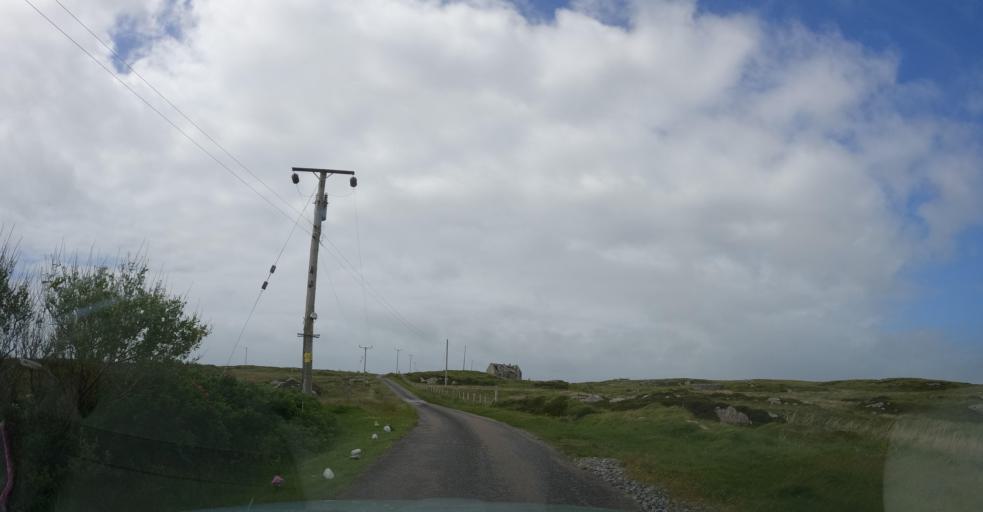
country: GB
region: Scotland
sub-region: Eilean Siar
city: Isle of South Uist
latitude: 57.2403
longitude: -7.3903
